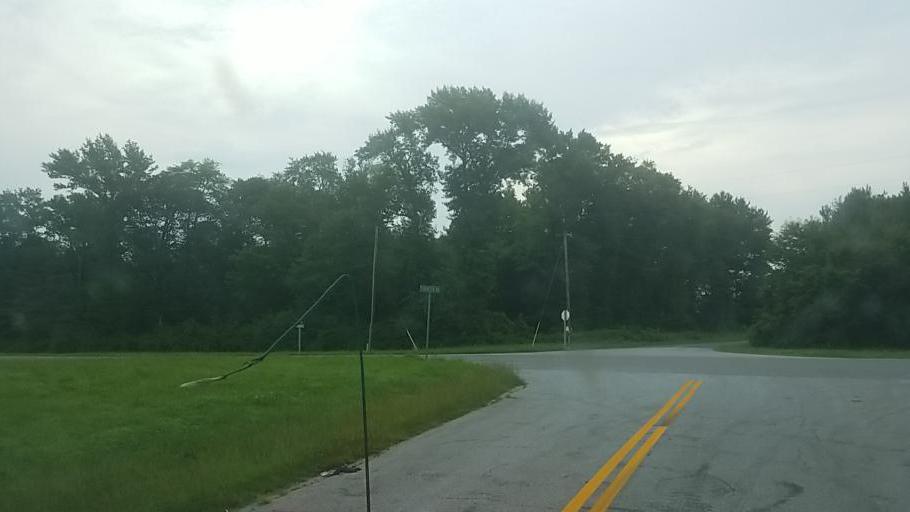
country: US
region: Delaware
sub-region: Sussex County
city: Selbyville
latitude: 38.4334
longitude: -75.2420
